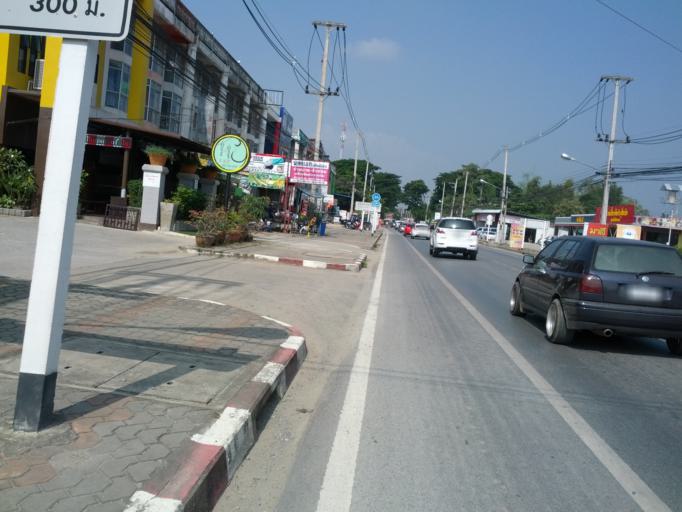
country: TH
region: Chiang Mai
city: San Kamphaeng
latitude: 18.7743
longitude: 99.0619
